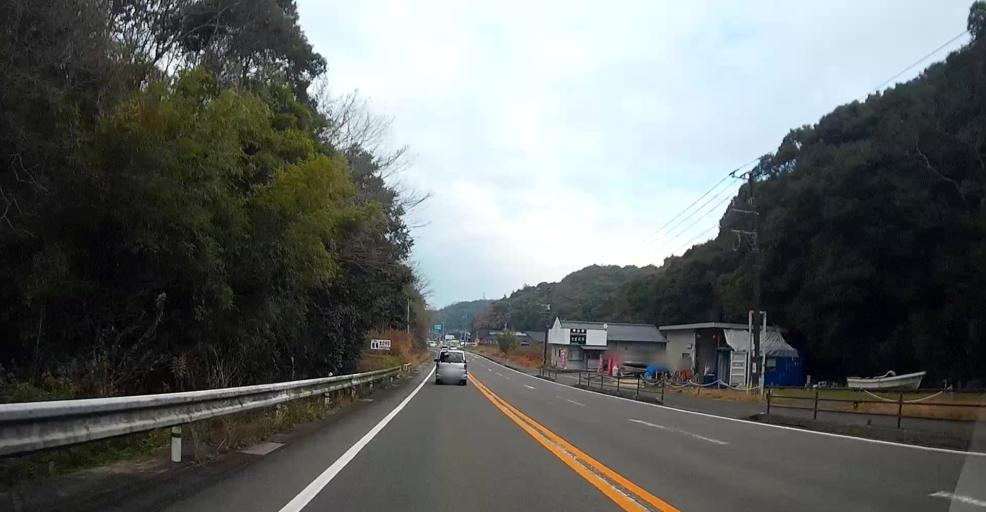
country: JP
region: Kumamoto
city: Yatsushiro
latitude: 32.5608
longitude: 130.4140
